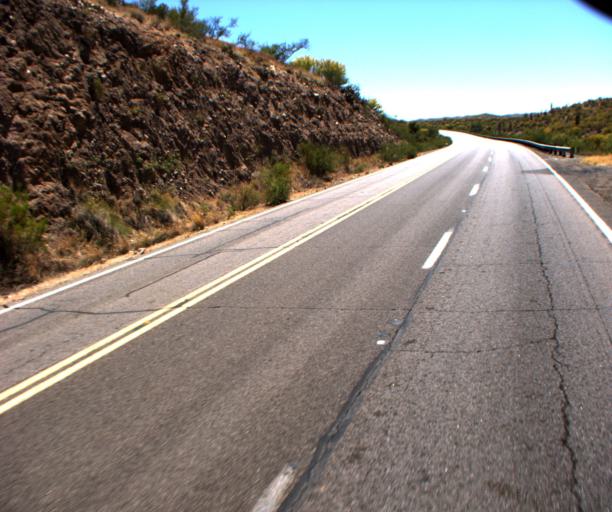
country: US
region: Arizona
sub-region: Pinal County
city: Mammoth
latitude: 32.6706
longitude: -110.6686
